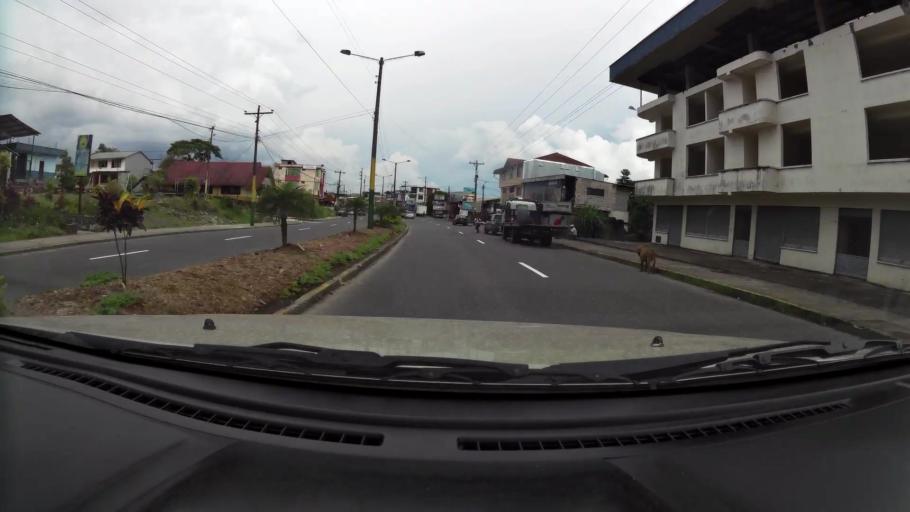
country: EC
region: Pastaza
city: Puyo
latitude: -1.4947
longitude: -78.0148
